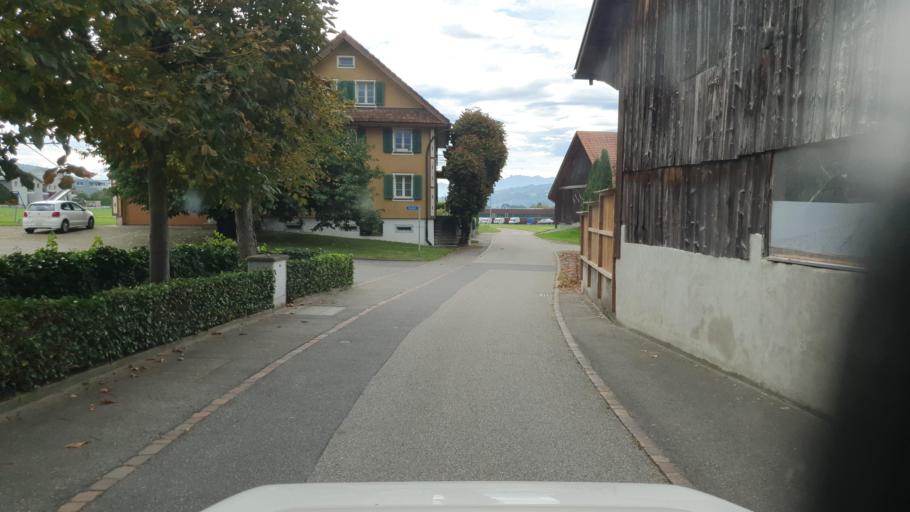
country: CH
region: Aargau
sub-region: Bezirk Lenzburg
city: Meisterschwanden
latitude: 47.2553
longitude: 8.2375
